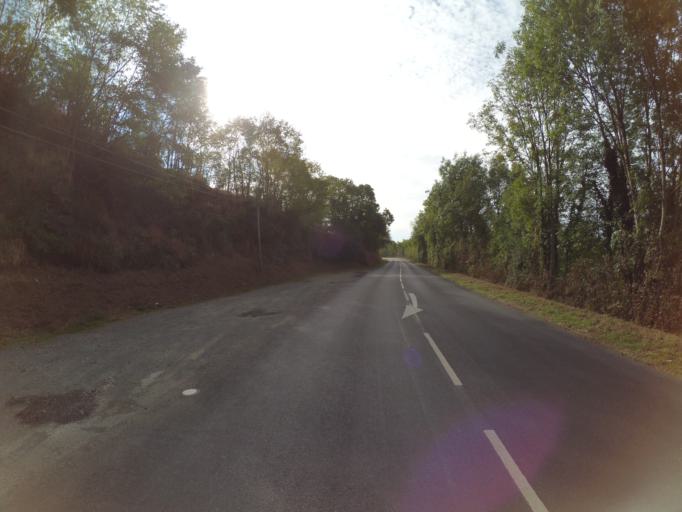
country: FR
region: Pays de la Loire
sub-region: Departement de Maine-et-Loire
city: La Chapelle-du-Genet
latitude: 47.1885
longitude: -1.0311
